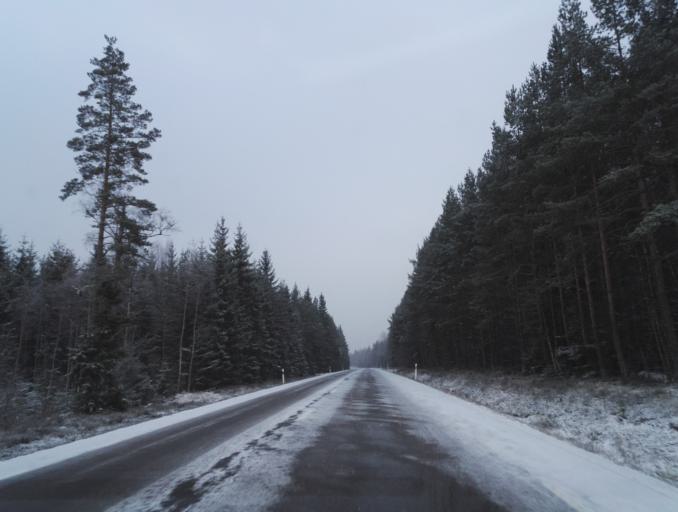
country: SE
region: Kronoberg
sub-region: Uppvidinge Kommun
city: Lenhovda
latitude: 56.8959
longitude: 15.3701
